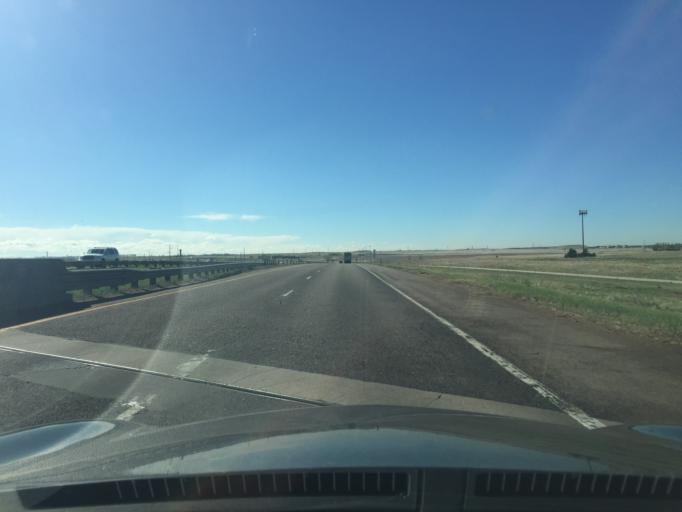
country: US
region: Colorado
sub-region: Adams County
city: Brighton
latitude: 39.9141
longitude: -104.7820
